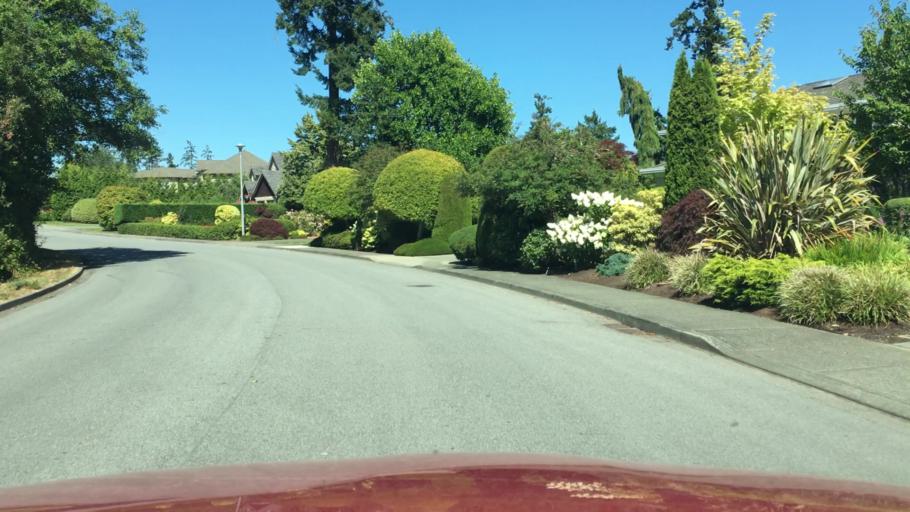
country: CA
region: British Columbia
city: North Saanich
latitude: 48.6749
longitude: -123.4220
